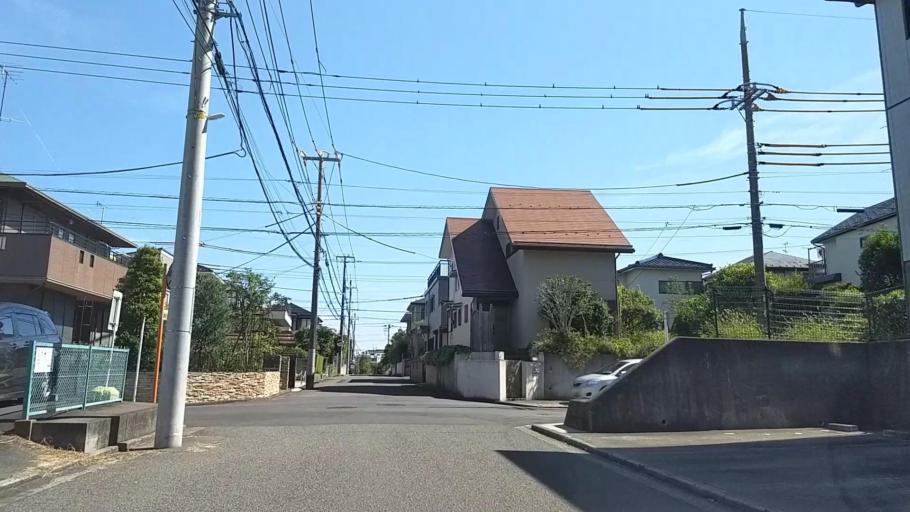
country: JP
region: Tokyo
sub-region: Machida-shi
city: Machida
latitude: 35.5555
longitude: 139.5520
